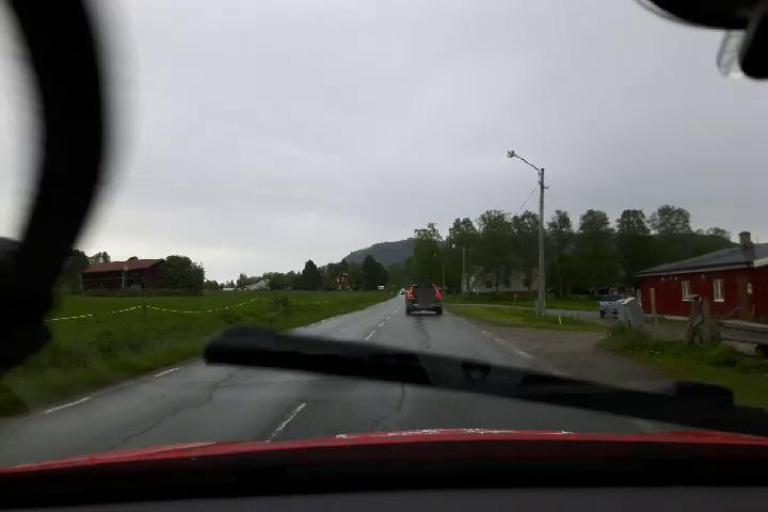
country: SE
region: Jaemtland
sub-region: Bergs Kommun
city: Hoverberg
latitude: 62.8038
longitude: 14.4377
